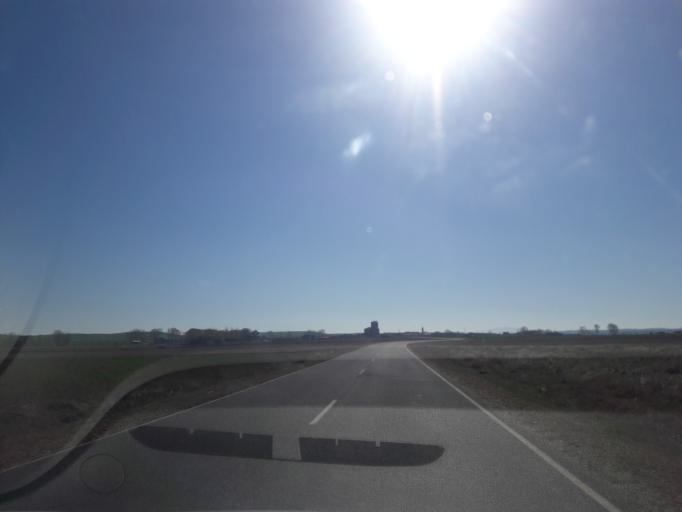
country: ES
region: Castille and Leon
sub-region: Provincia de Salamanca
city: Salmoral
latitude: 40.8055
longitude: -5.2305
